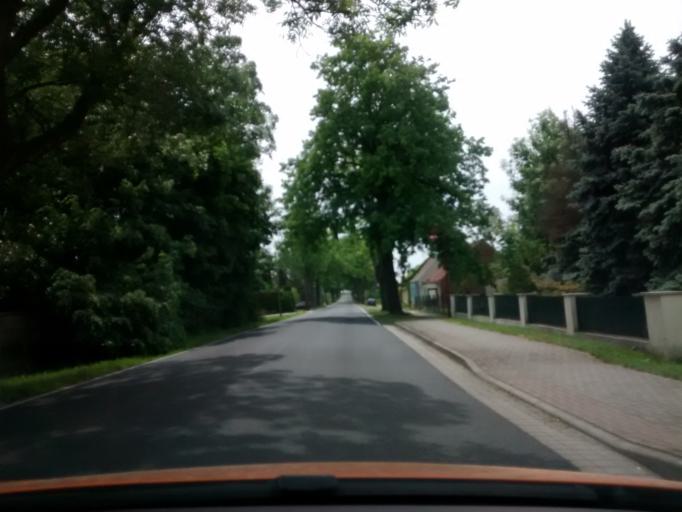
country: DE
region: Brandenburg
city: Juterbog
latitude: 51.9308
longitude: 13.1231
